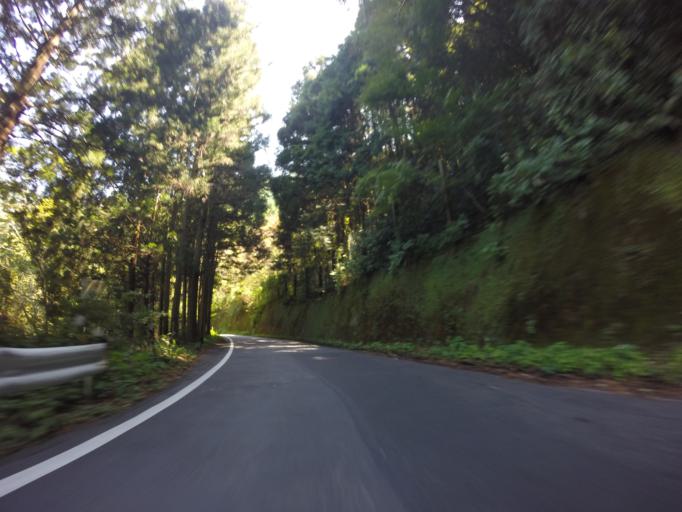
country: JP
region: Shizuoka
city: Shizuoka-shi
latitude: 35.0336
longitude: 138.2579
